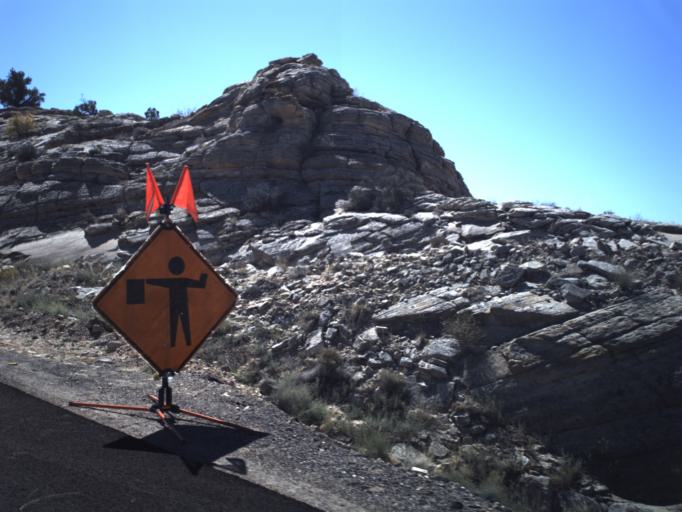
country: US
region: Utah
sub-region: Wayne County
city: Loa
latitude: 37.8325
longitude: -111.4156
